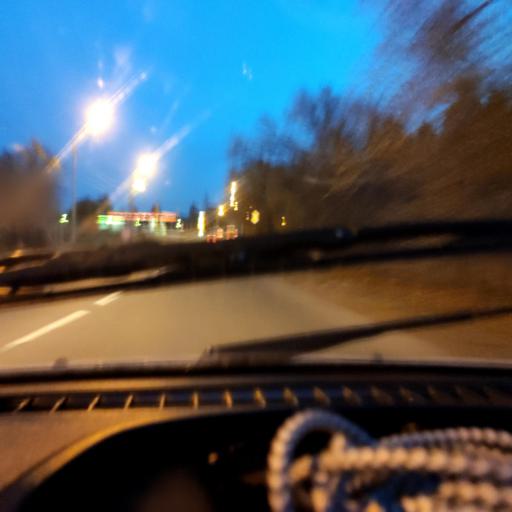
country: RU
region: Samara
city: Zhigulevsk
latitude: 53.4690
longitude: 49.5469
